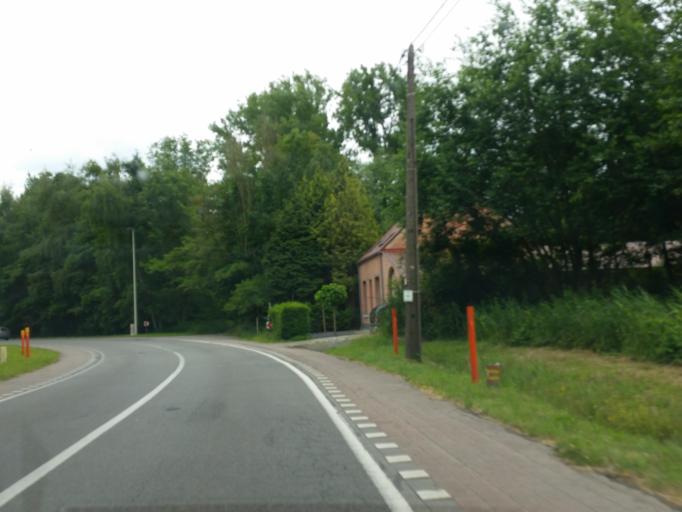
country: BE
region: Flanders
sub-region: Provincie Antwerpen
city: Ranst
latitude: 51.1997
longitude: 4.5985
